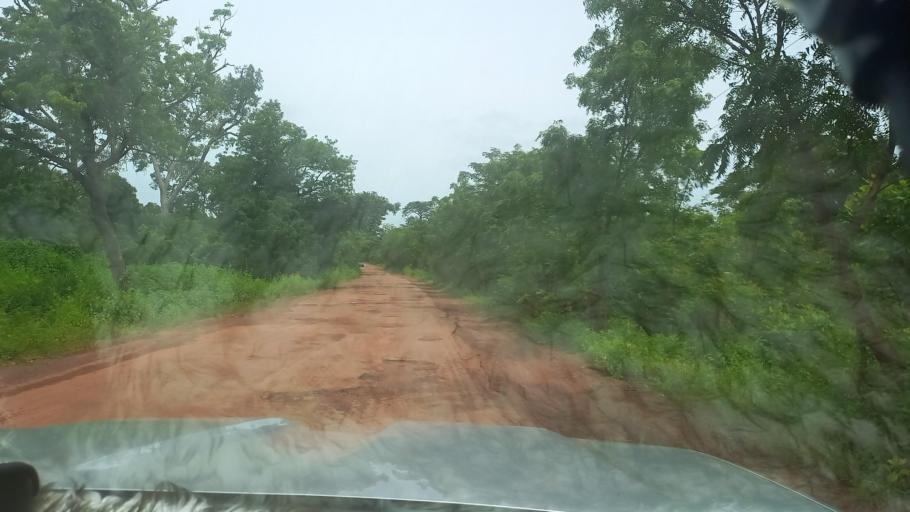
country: SN
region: Kolda
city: Marsassoum
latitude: 12.9109
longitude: -16.0111
